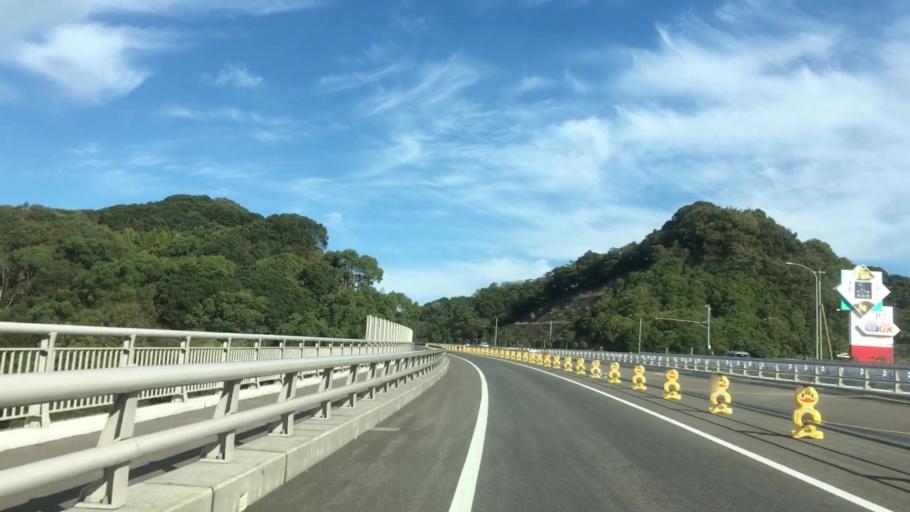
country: JP
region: Nagasaki
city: Sasebo
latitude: 33.1192
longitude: 129.7925
